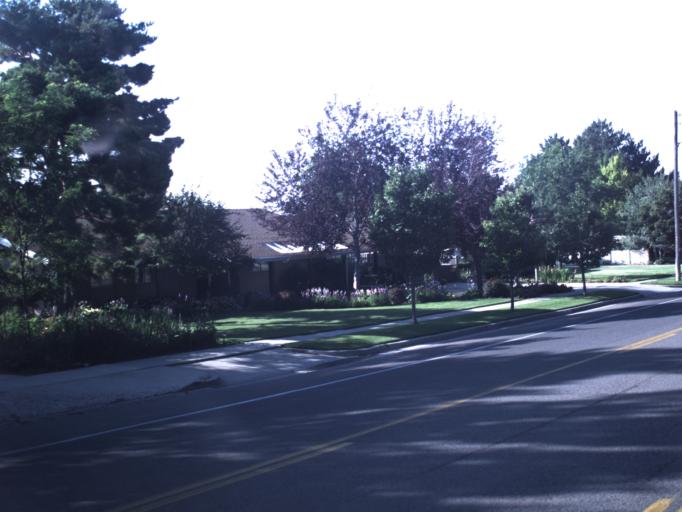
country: US
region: Utah
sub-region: Utah County
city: American Fork
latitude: 40.3985
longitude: -111.7953
